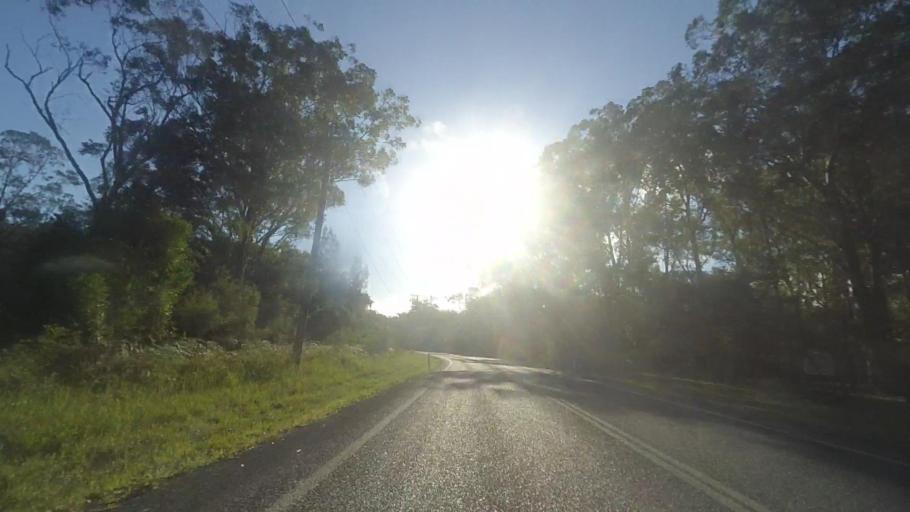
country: AU
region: New South Wales
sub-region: Great Lakes
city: Nabiac
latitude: -32.0894
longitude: 152.4632
